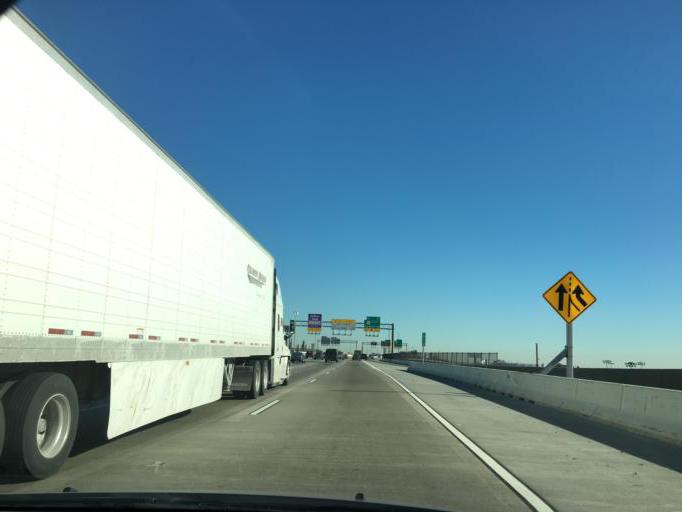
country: US
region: Maryland
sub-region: City of Baltimore
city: Baltimore
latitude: 39.2672
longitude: -76.6218
